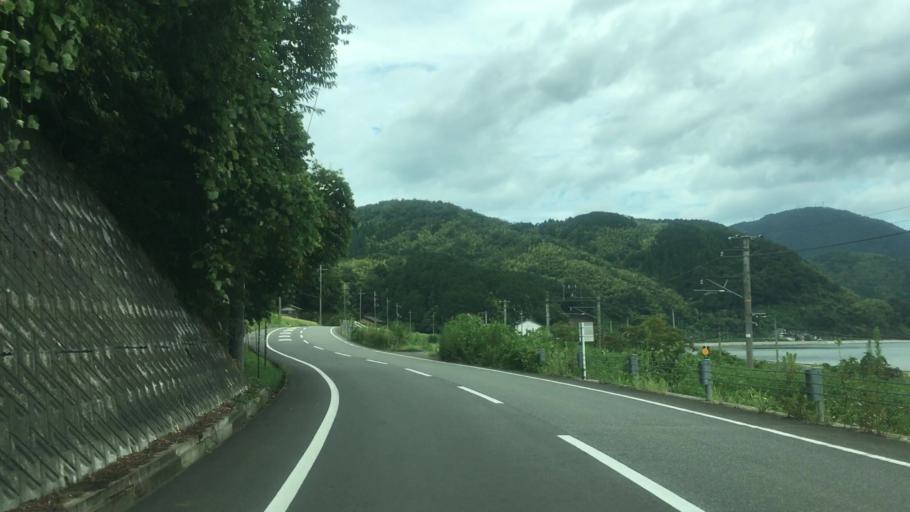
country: JP
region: Hyogo
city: Toyooka
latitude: 35.5759
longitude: 134.8037
